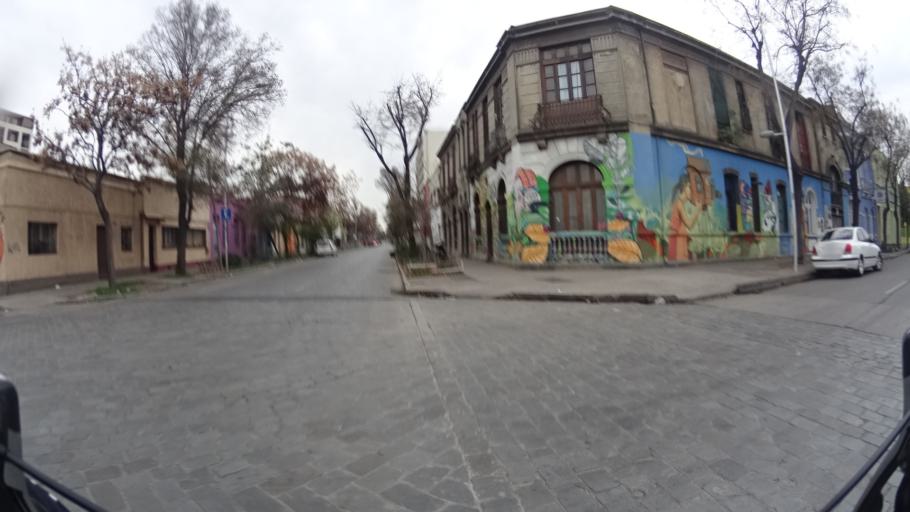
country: CL
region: Santiago Metropolitan
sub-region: Provincia de Santiago
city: Santiago
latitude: -33.4563
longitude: -70.6641
